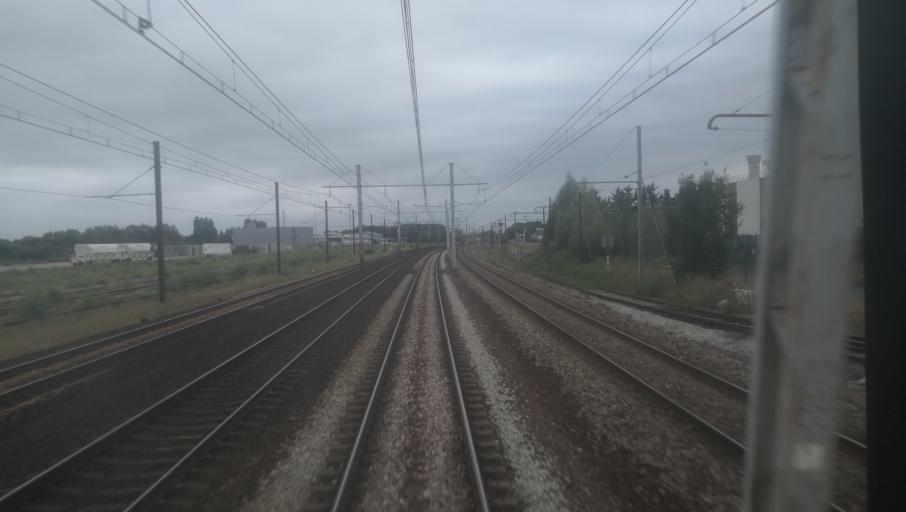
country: FR
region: Ile-de-France
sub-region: Departement de l'Essonne
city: Marolles-en-Hurepoix
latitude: 48.5799
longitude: 2.2900
